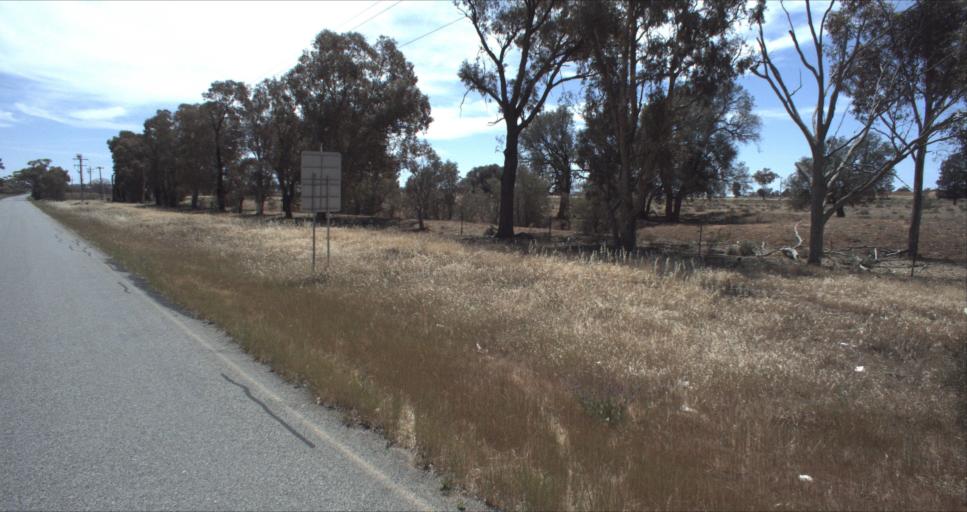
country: AU
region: New South Wales
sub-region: Leeton
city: Leeton
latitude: -34.6436
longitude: 146.4693
